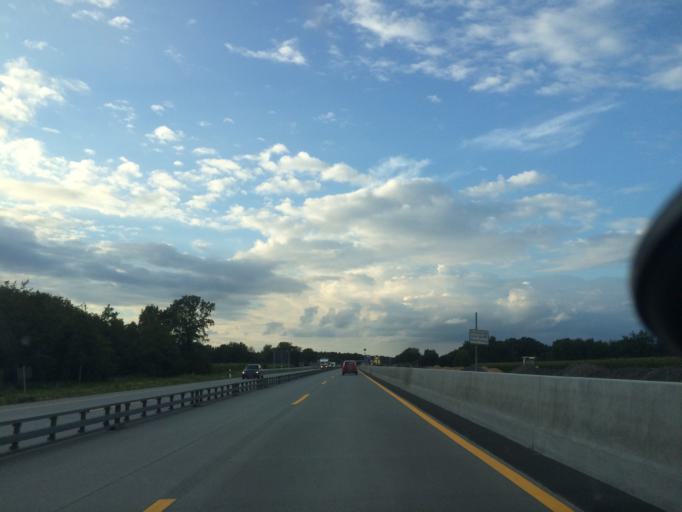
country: DE
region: Schleswig-Holstein
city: Grossenaspe
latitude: 53.9943
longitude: 9.9372
